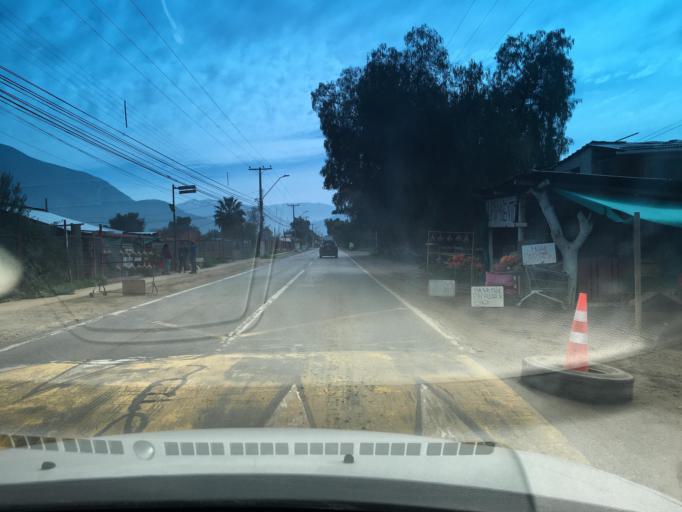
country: CL
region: Santiago Metropolitan
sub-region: Provincia de Chacabuco
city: Lampa
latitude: -33.0956
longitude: -70.9293
